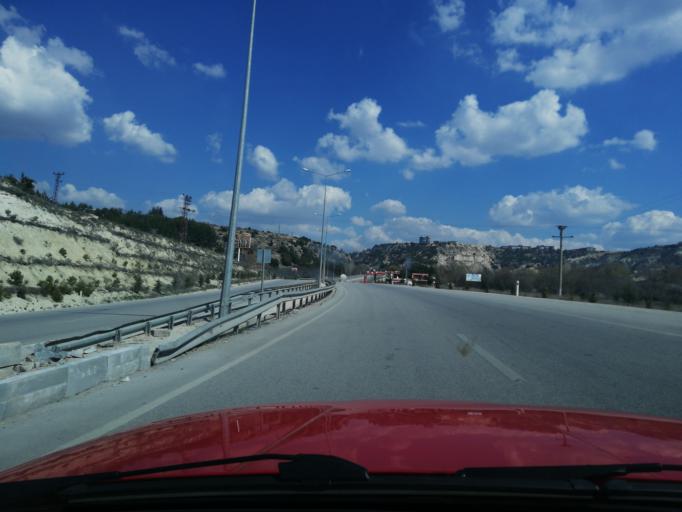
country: TR
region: Burdur
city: Burdur
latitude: 37.6989
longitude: 30.3227
